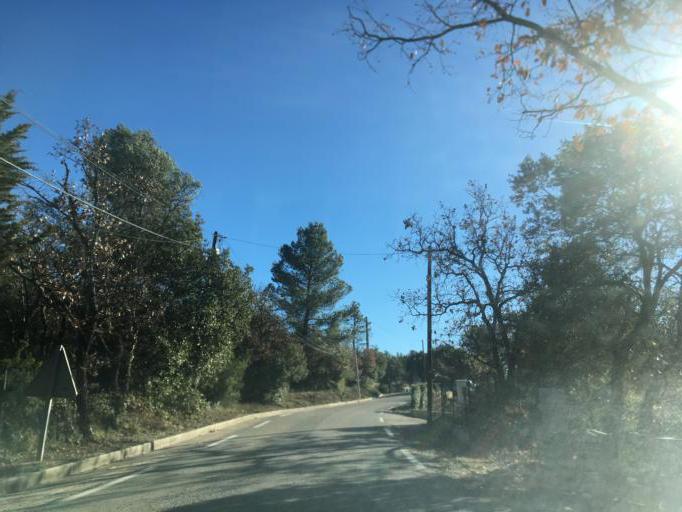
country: FR
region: Provence-Alpes-Cote d'Azur
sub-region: Departement du Var
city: Barjols
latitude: 43.5942
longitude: 6.0337
